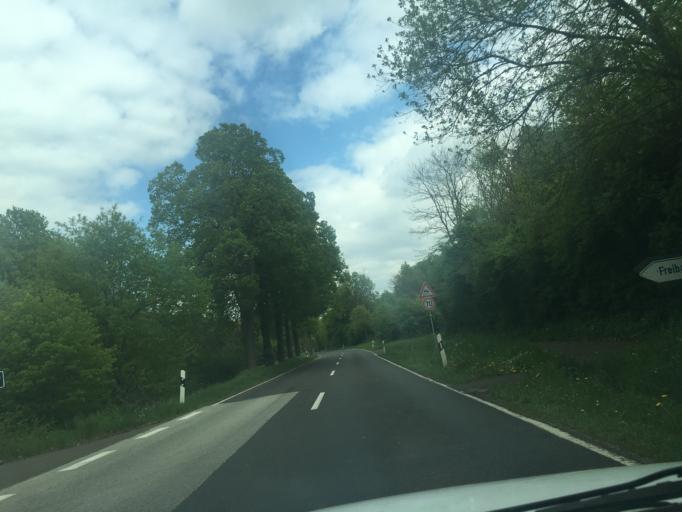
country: DE
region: Rheinland-Pfalz
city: Mengerschied
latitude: 49.8992
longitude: 7.4892
